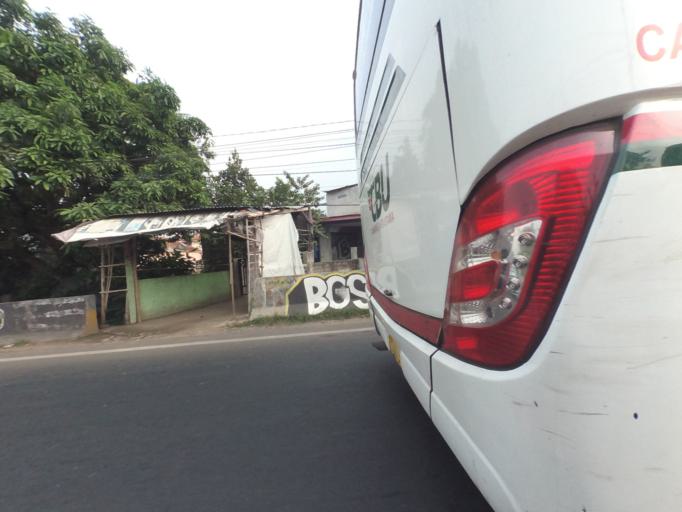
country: ID
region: West Java
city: Ciampea
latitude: -6.5664
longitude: 106.6730
